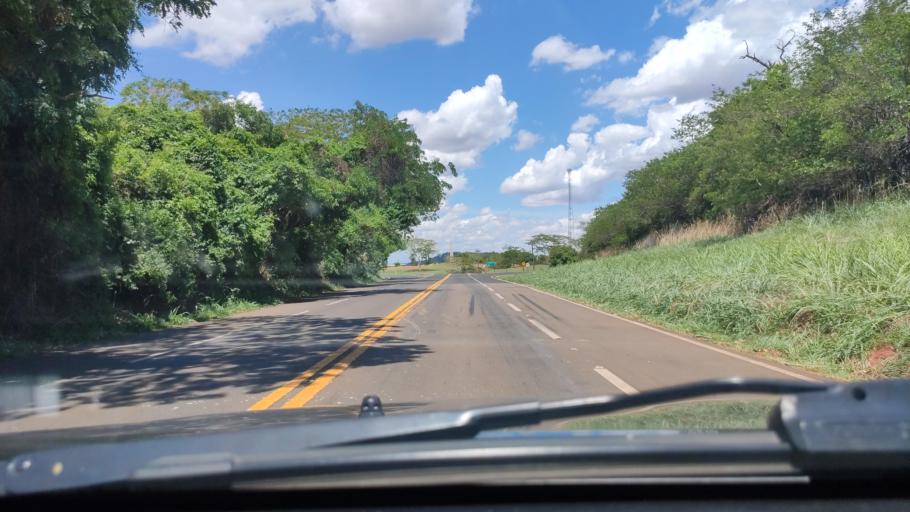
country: BR
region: Sao Paulo
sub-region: Boa Esperanca Do Sul
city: Boa Esperanca do Sul
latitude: -22.0699
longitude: -48.4299
